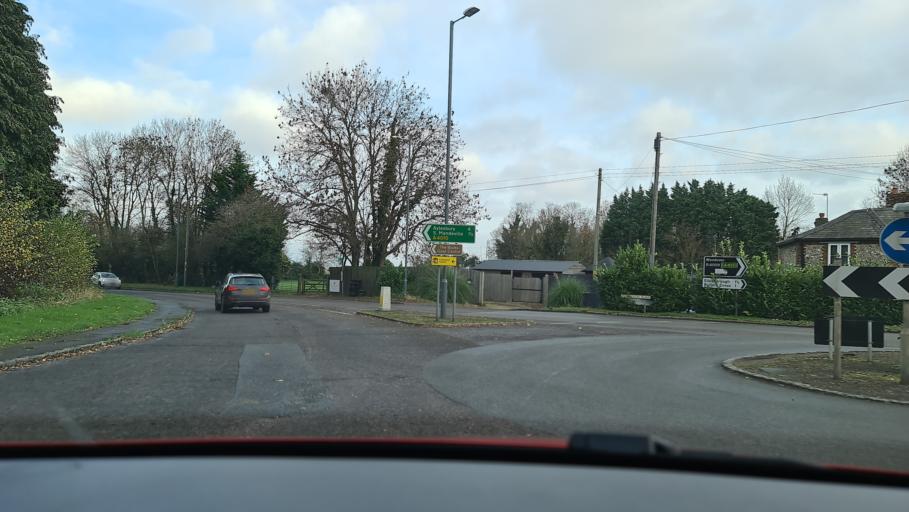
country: GB
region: England
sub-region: Buckinghamshire
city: Weston Turville
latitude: 51.7660
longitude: -0.7854
